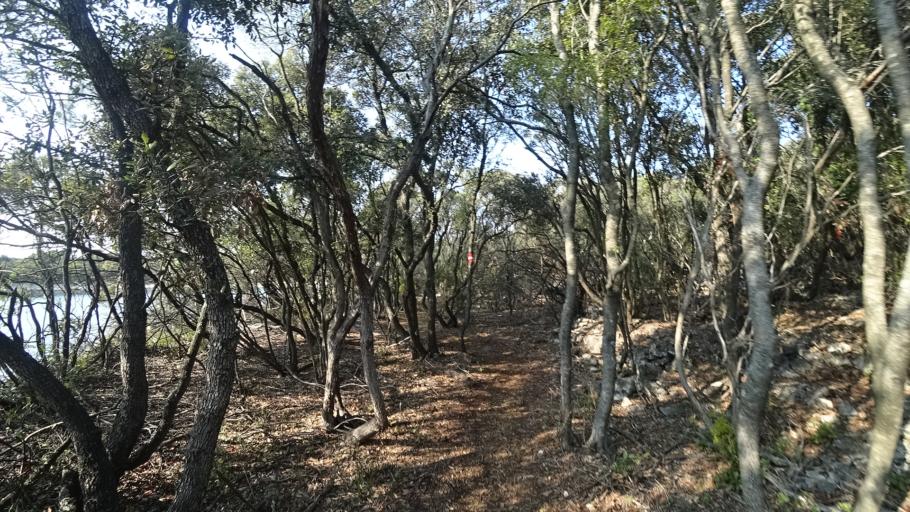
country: HR
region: Primorsko-Goranska
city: Mali Losinj
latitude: 44.4870
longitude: 14.5089
